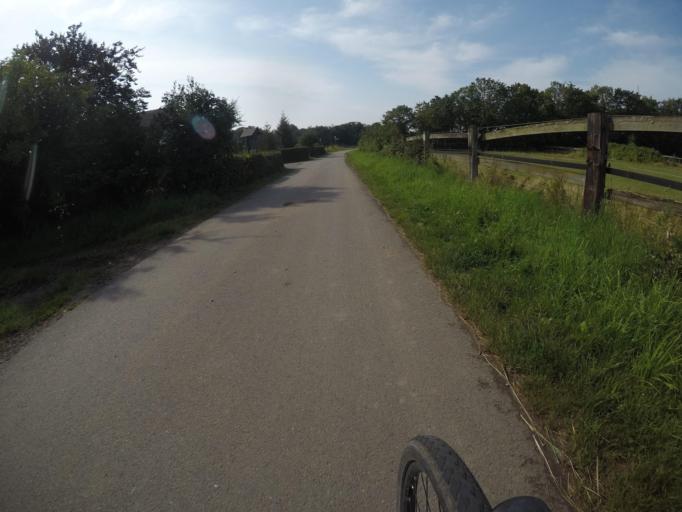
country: DE
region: Baden-Wuerttemberg
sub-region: Karlsruhe Region
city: Plankstadt
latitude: 49.4257
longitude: 8.5720
